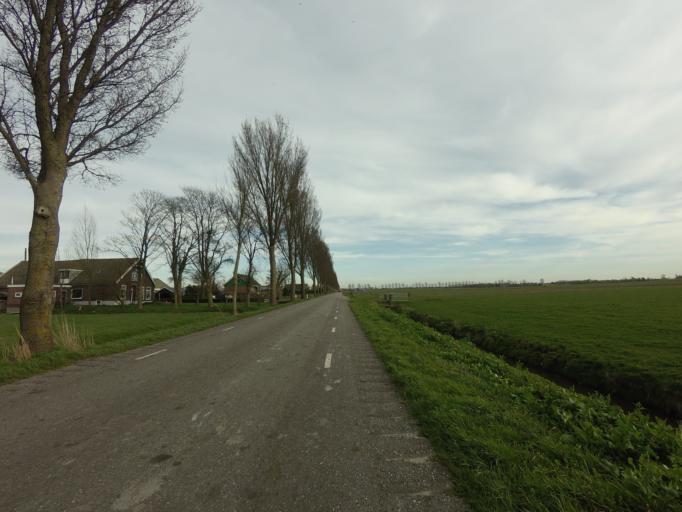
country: NL
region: Utrecht
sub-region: Gemeente De Ronde Venen
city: Mijdrecht
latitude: 52.1983
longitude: 4.8348
